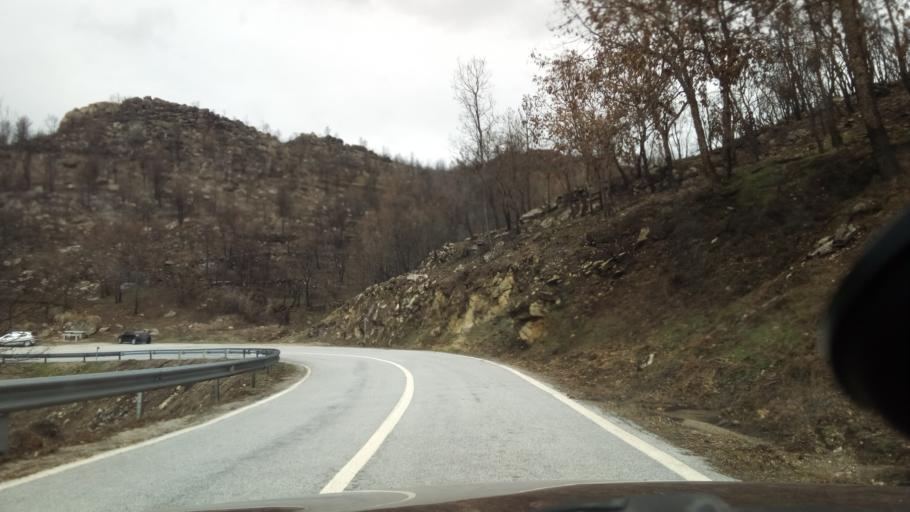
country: PT
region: Guarda
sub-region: Manteigas
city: Manteigas
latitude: 40.4729
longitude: -7.5931
